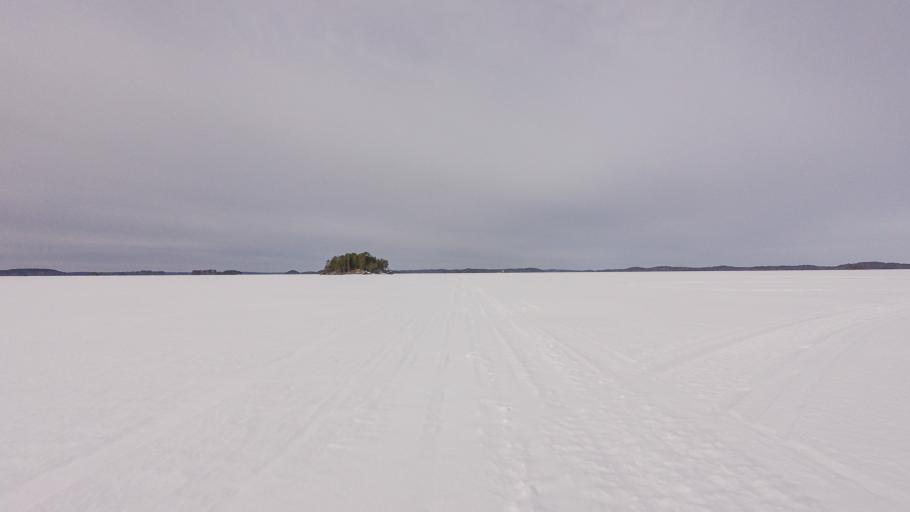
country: FI
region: Southern Savonia
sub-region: Savonlinna
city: Rantasalmi
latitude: 62.1042
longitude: 28.4253
